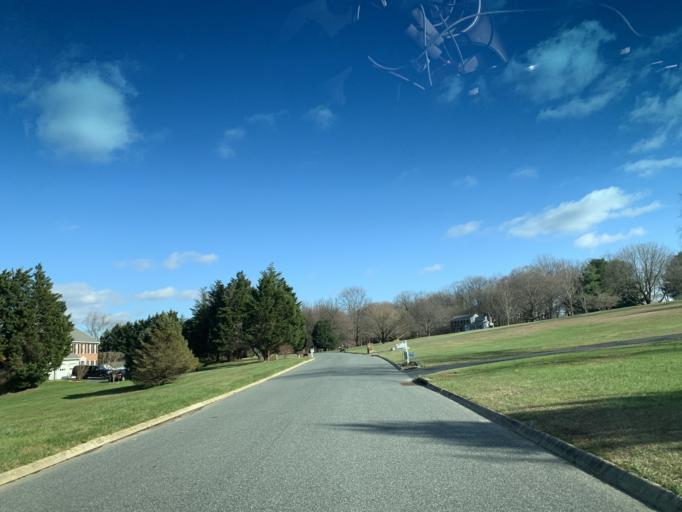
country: US
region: Maryland
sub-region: Harford County
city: Bel Air South
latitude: 39.5337
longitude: -76.2795
